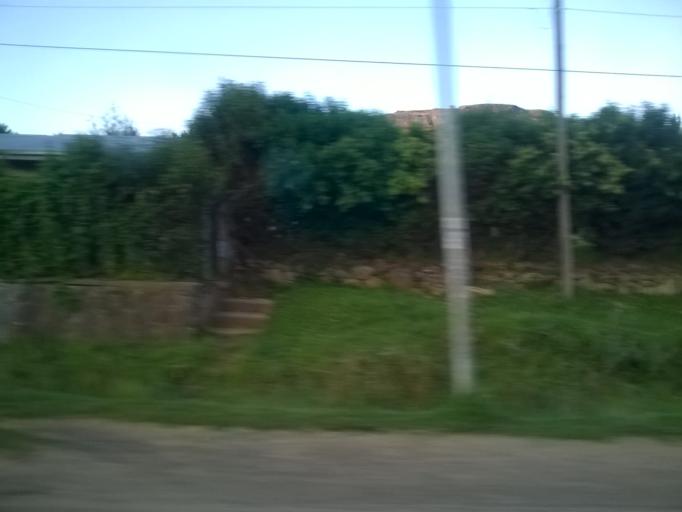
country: LS
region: Leribe
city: Leribe
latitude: -28.8674
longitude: 28.0680
